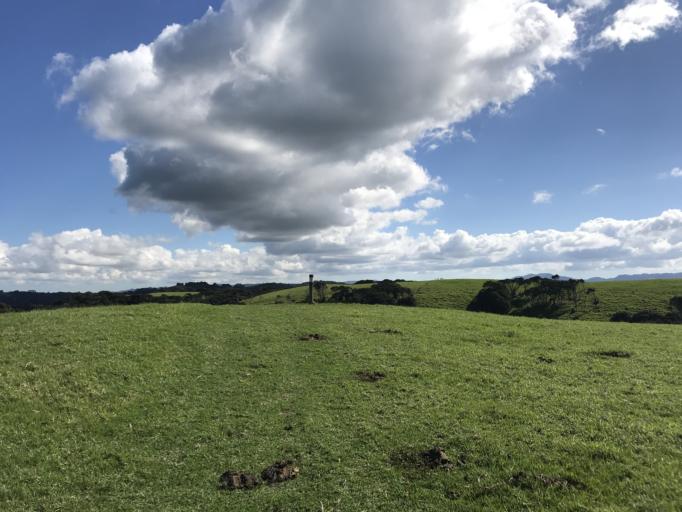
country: NZ
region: Auckland
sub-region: Auckland
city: Warkworth
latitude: -36.3760
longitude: 174.8360
